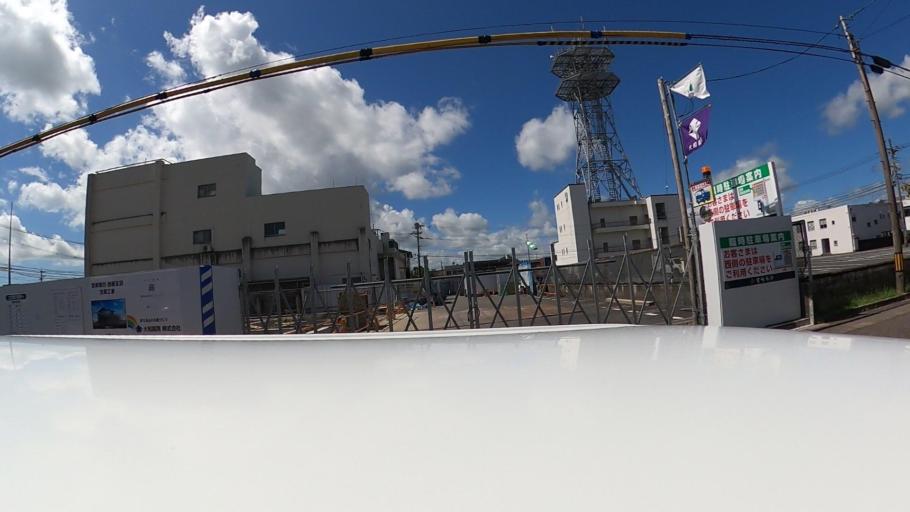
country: JP
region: Miyazaki
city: Tsuma
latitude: 32.1096
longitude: 131.4028
